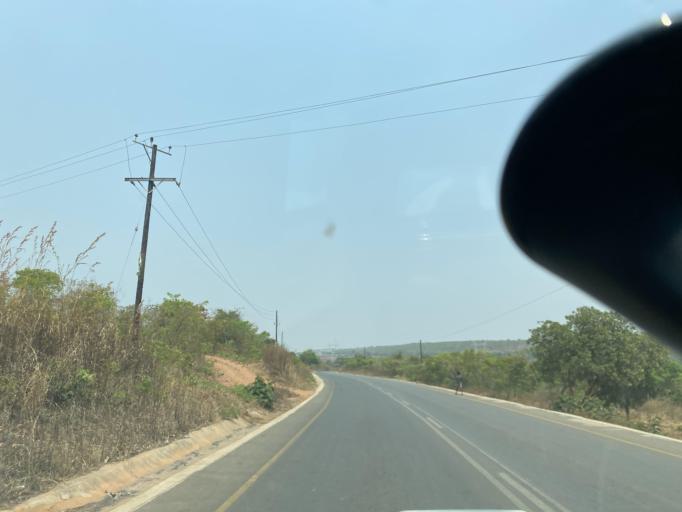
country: ZM
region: Lusaka
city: Lusaka
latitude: -15.5420
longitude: 28.4741
